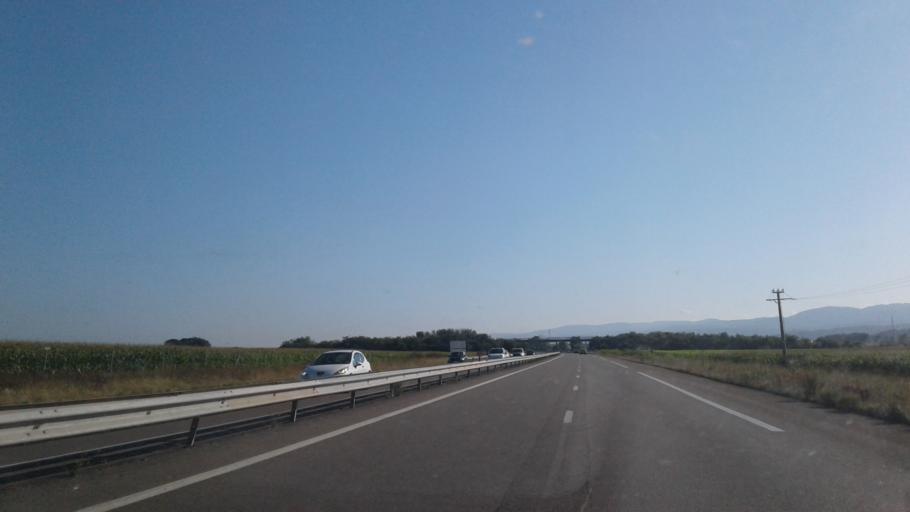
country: FR
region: Rhone-Alpes
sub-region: Departement de l'Ain
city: Leyment
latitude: 45.9226
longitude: 5.2649
